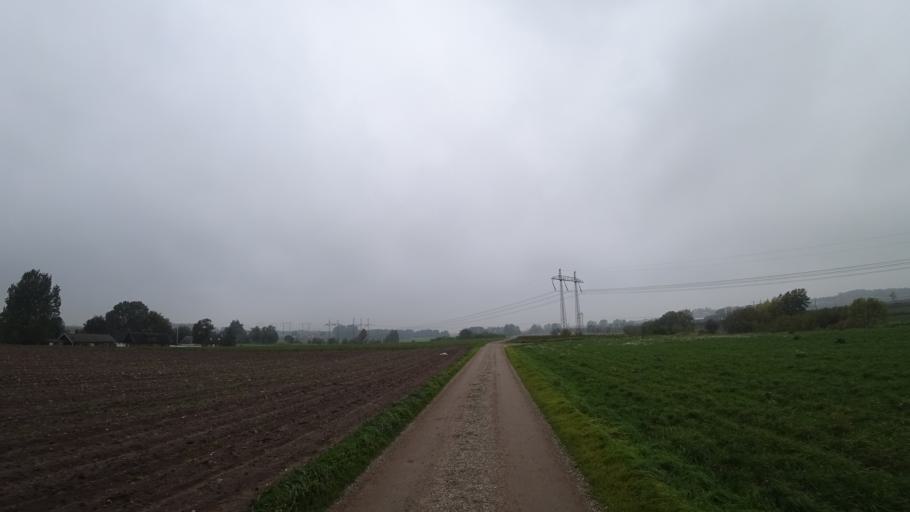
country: SE
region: Skane
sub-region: Kavlinge Kommun
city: Kaevlinge
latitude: 55.8152
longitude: 13.0834
